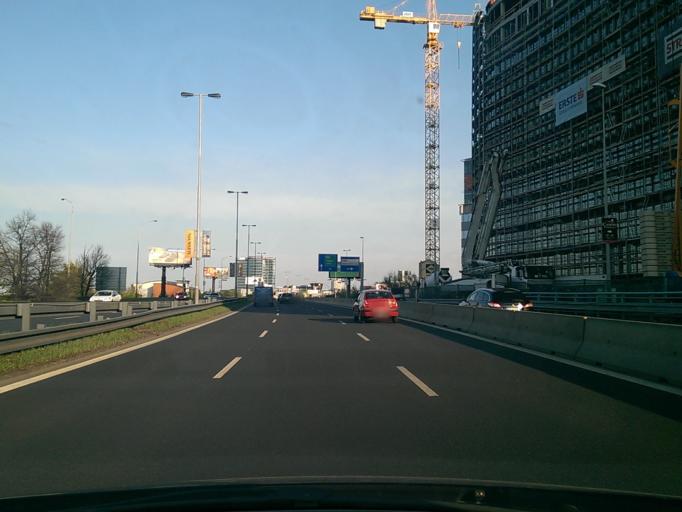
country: CZ
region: Praha
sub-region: Praha 2
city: Vysehrad
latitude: 50.0528
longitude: 14.4414
